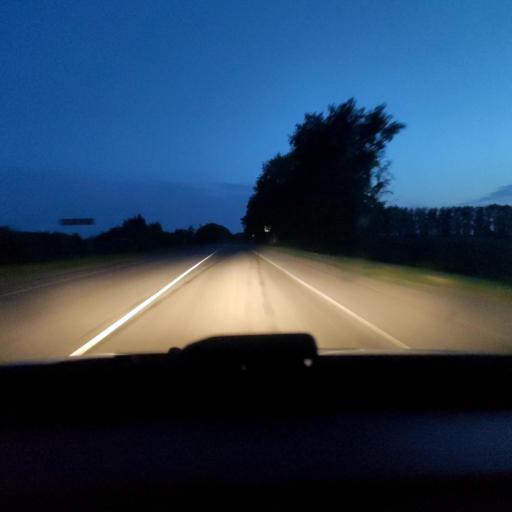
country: RU
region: Voronezj
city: Panino
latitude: 51.6263
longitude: 40.0402
